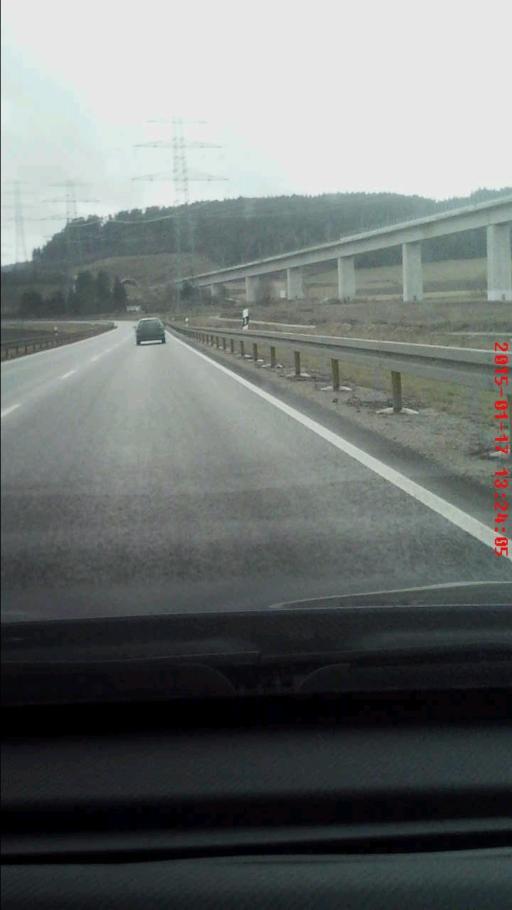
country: DE
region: Thuringia
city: Langewiesen
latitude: 50.6674
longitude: 10.9904
